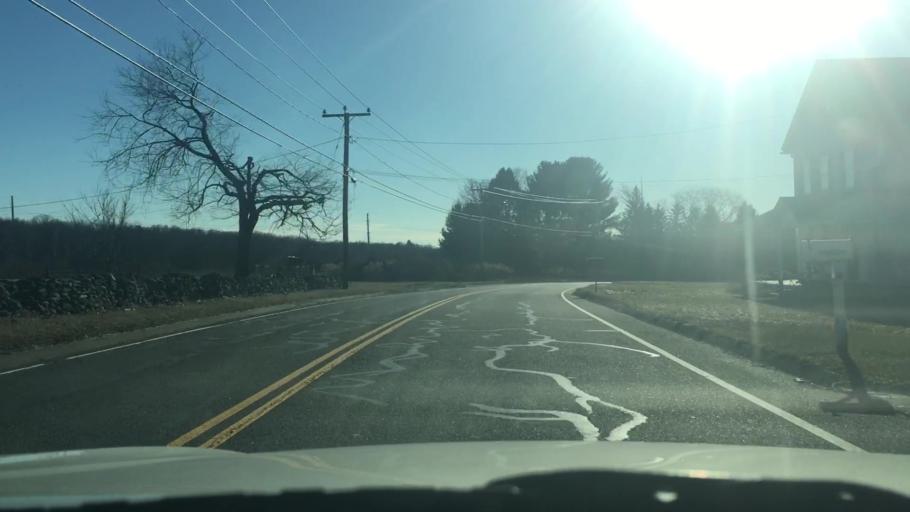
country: US
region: Massachusetts
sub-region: Hampden County
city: Ludlow
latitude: 42.1927
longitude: -72.4992
